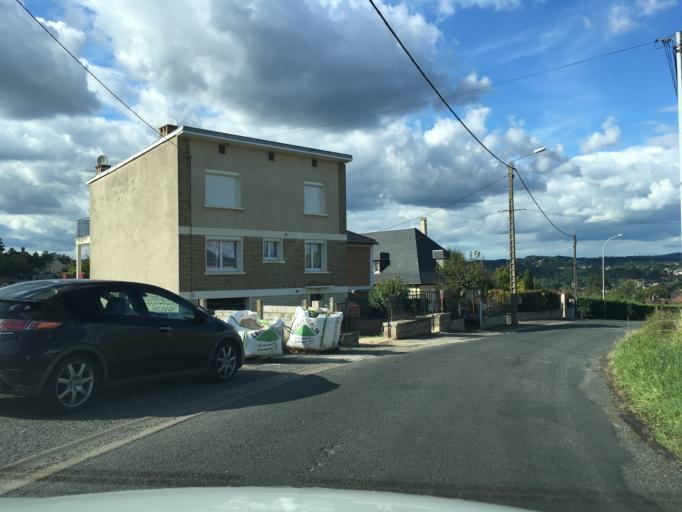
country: FR
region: Limousin
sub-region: Departement de la Correze
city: Malemort-sur-Correze
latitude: 45.1492
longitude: 1.5577
